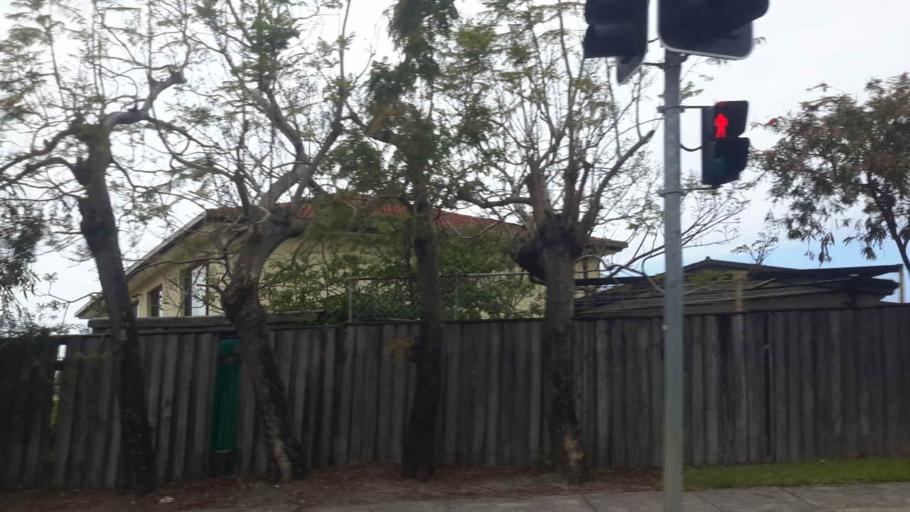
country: AU
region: New South Wales
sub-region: Wollongong
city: Bulli
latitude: -34.3531
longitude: 150.9025
